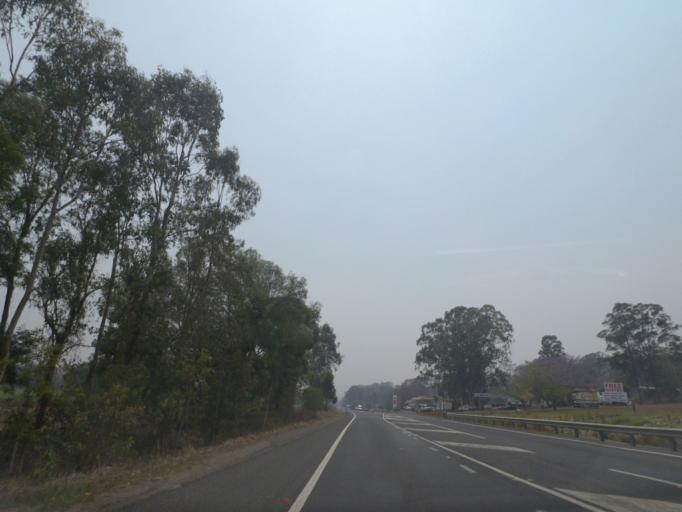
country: AU
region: New South Wales
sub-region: Clarence Valley
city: Maclean
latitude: -29.5622
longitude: 153.1482
